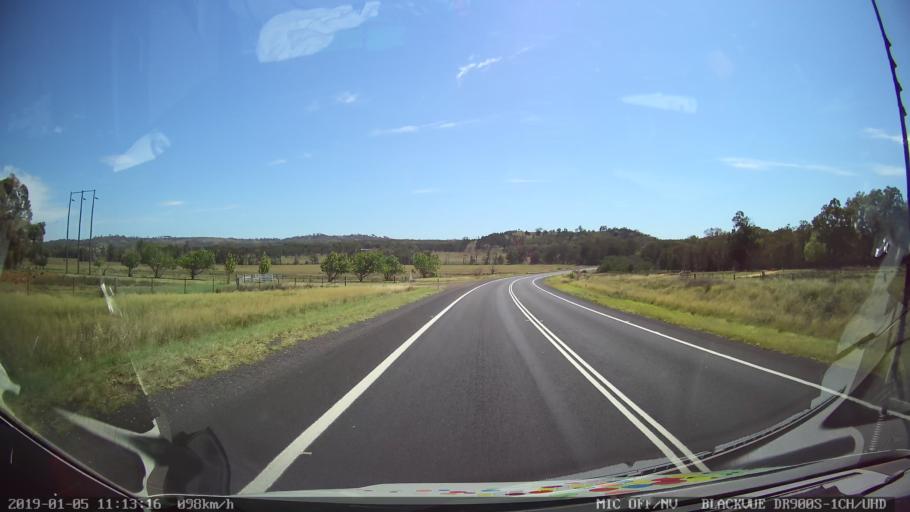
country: AU
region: New South Wales
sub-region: Warrumbungle Shire
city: Coonabarabran
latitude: -31.3722
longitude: 149.2686
